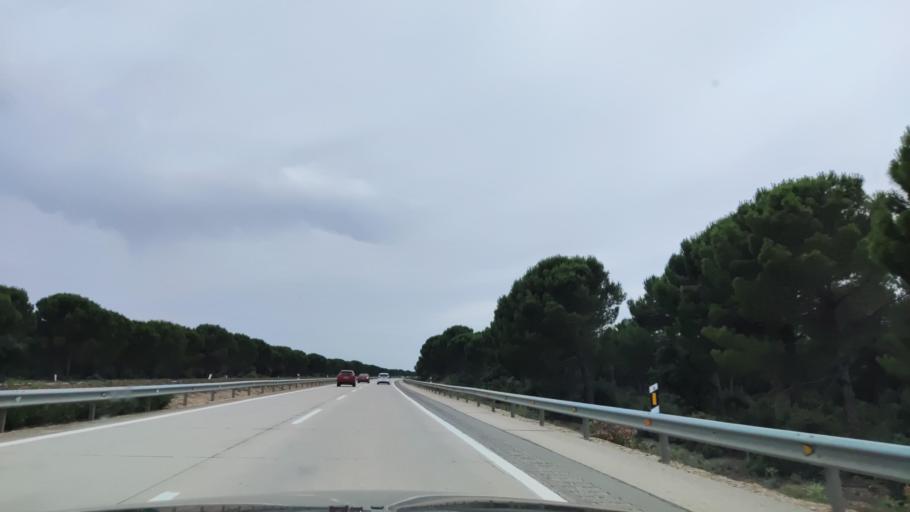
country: ES
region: Castille-La Mancha
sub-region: Provincia de Cuenca
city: Pozoamargo
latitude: 39.3409
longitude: -2.1995
